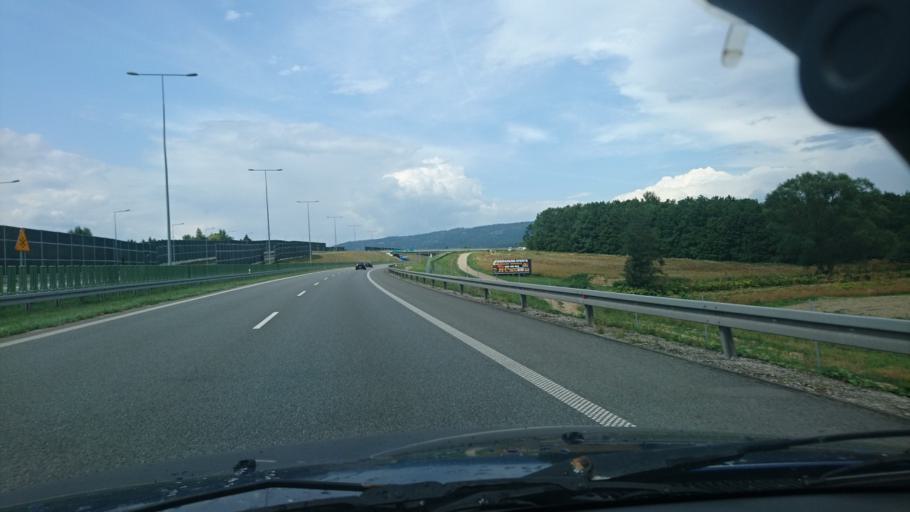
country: PL
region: Silesian Voivodeship
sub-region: Powiat bielski
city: Rybarzowice
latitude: 49.7084
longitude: 19.1206
